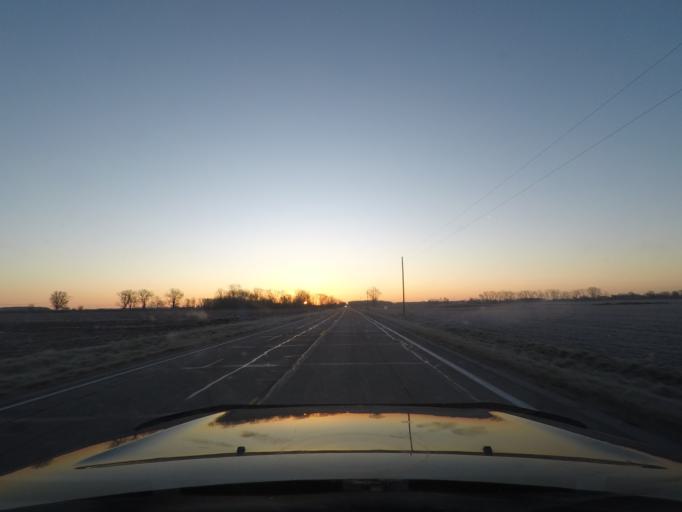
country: US
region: Indiana
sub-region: Saint Joseph County
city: Walkerton
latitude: 41.4763
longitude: -86.5687
